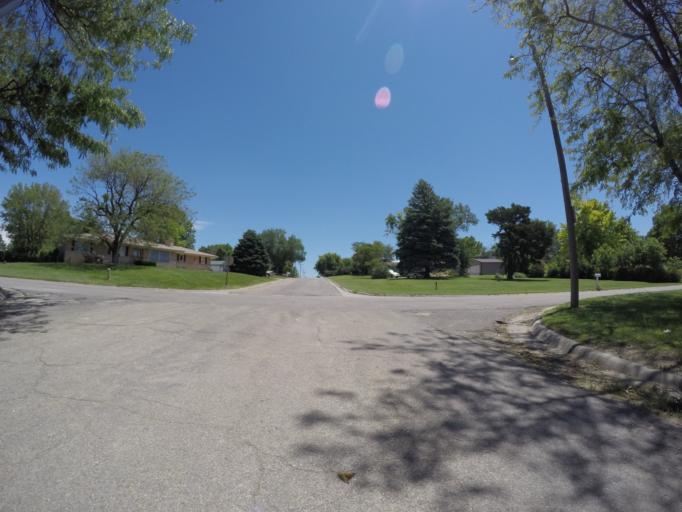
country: US
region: Kansas
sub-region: Jewell County
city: Mankato
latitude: 39.7868
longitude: -98.2037
